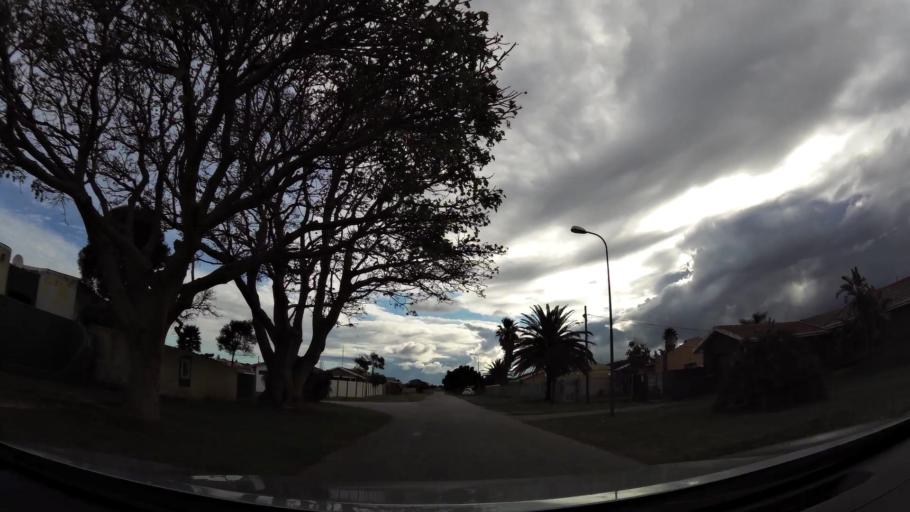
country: ZA
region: Eastern Cape
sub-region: Nelson Mandela Bay Metropolitan Municipality
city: Port Elizabeth
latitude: -33.9361
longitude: 25.4667
